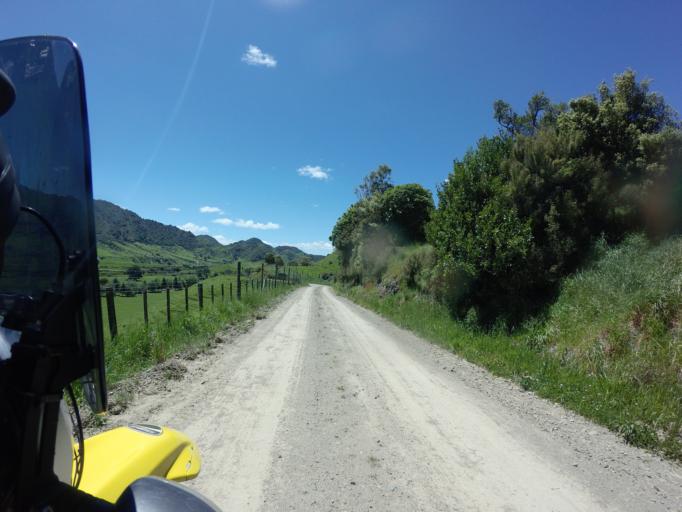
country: NZ
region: Bay of Plenty
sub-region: Opotiki District
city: Opotiki
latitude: -38.4017
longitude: 177.4563
